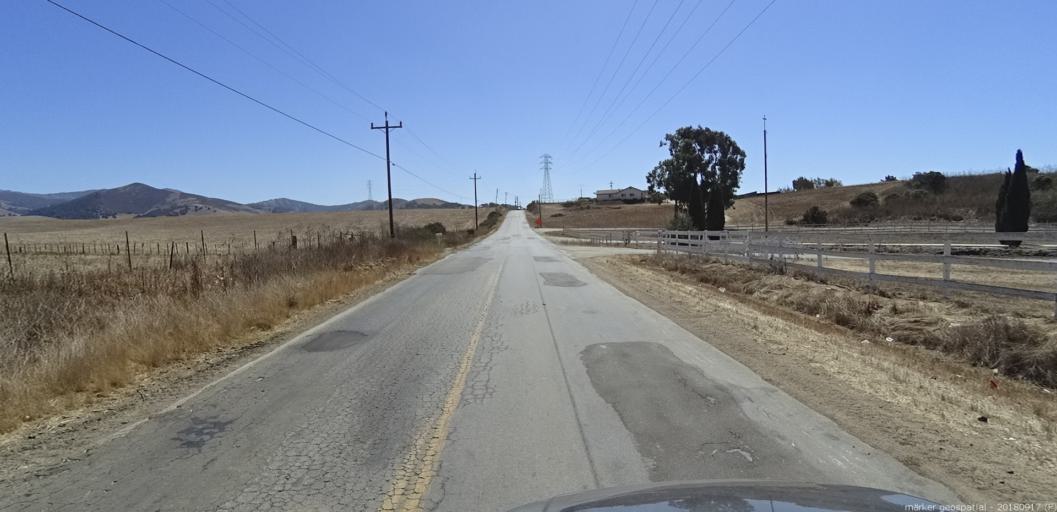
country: US
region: California
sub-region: Monterey County
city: Salinas
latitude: 36.7041
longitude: -121.5793
